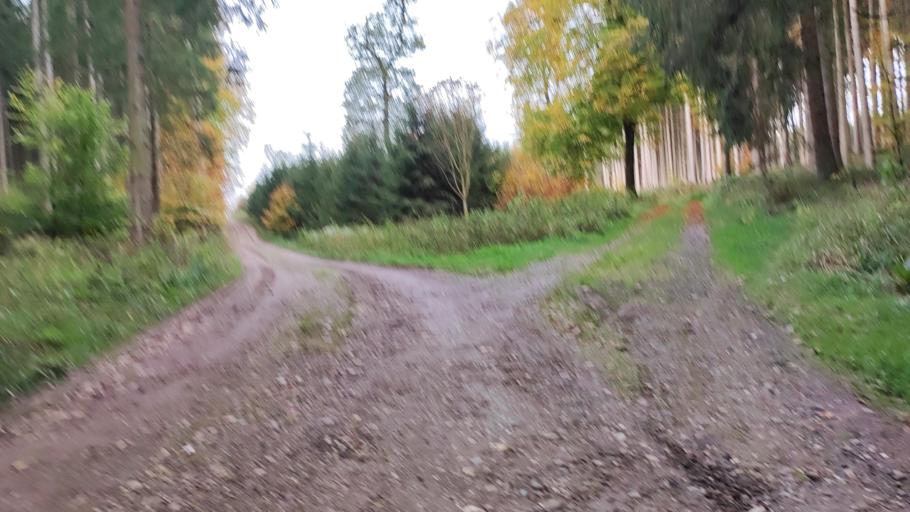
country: DE
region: Bavaria
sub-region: Swabia
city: Ziemetshausen
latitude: 48.3451
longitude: 10.5298
